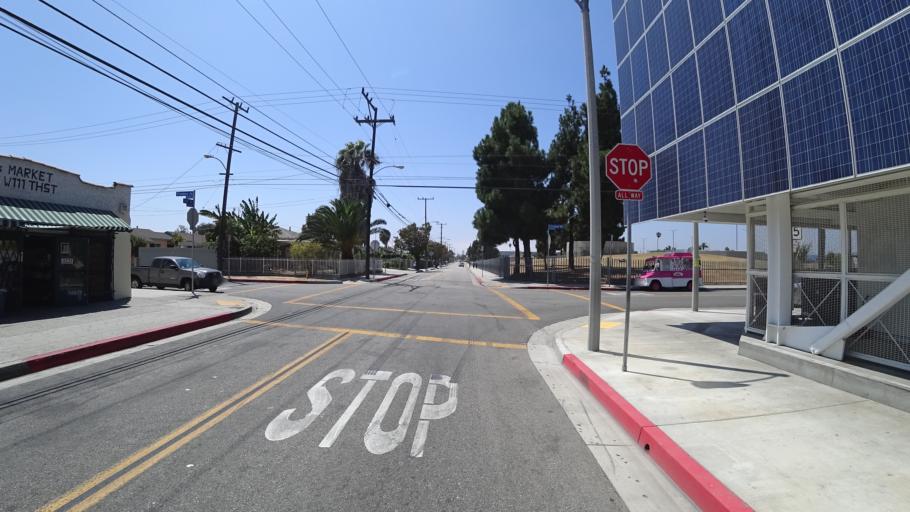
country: US
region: California
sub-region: Los Angeles County
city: Lennox
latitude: 33.9346
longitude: -118.3480
